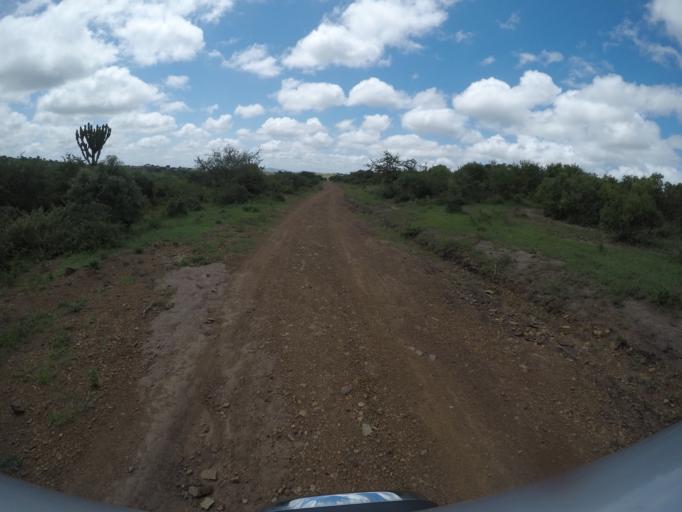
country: ZA
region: KwaZulu-Natal
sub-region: uThungulu District Municipality
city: Empangeni
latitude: -28.5848
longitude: 31.8295
